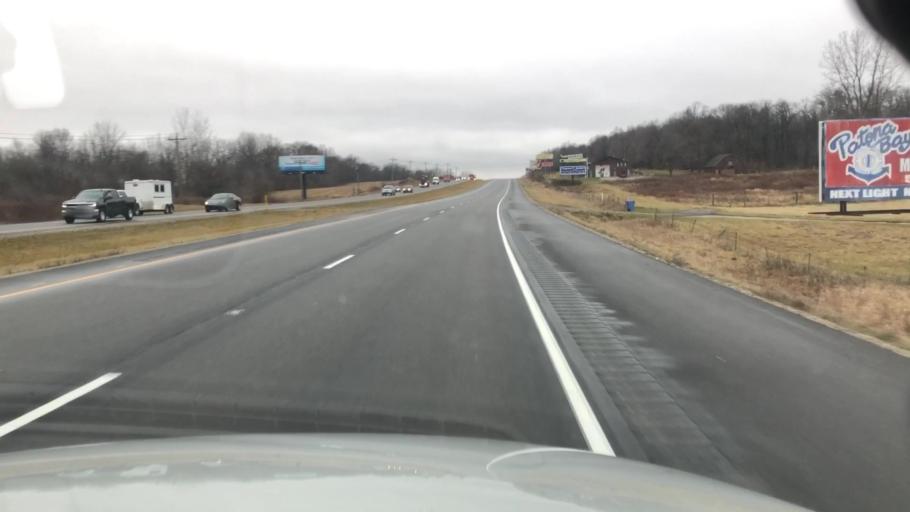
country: US
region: Indiana
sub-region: Kosciusko County
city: Pierceton
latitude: 41.1821
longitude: -85.6325
